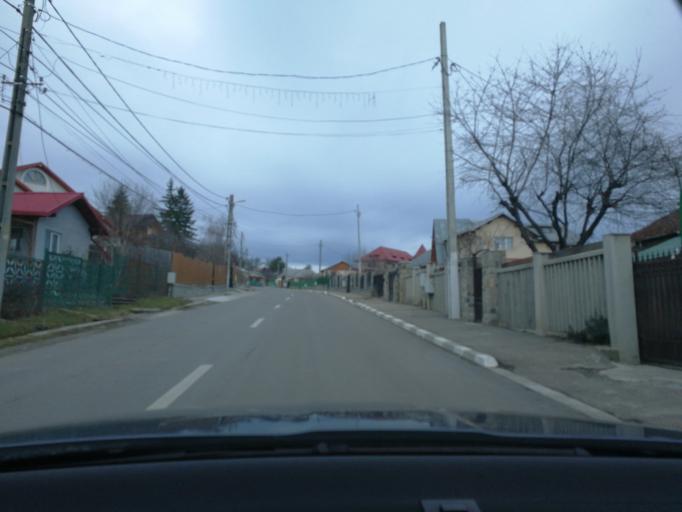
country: RO
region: Prahova
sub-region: Municipiul Campina
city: Campina
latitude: 45.1279
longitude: 25.7093
